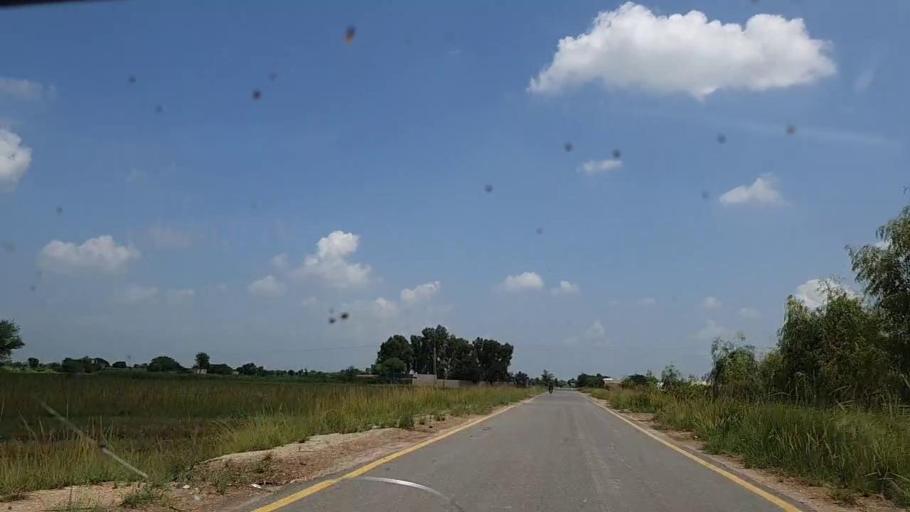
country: PK
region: Sindh
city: Tharu Shah
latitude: 26.9734
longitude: 68.0889
